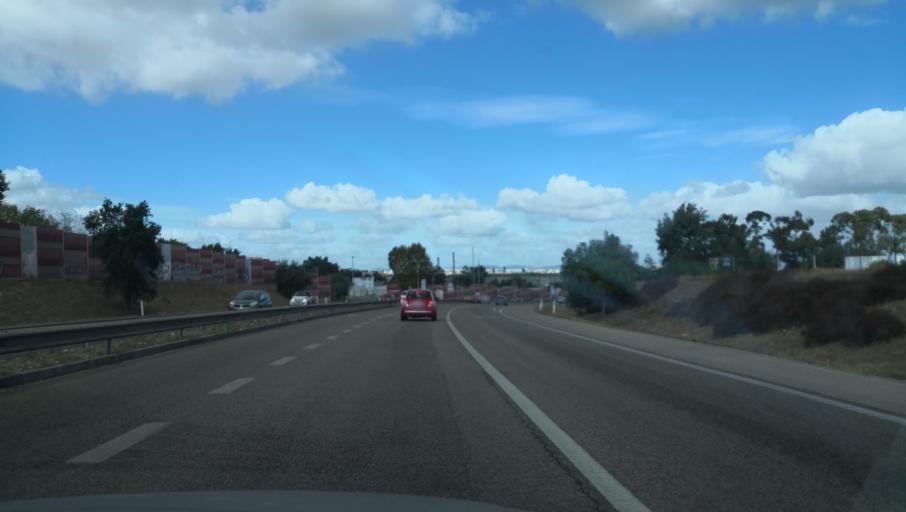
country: PT
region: Setubal
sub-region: Barreiro
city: Barreiro
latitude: 38.6550
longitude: -9.0548
